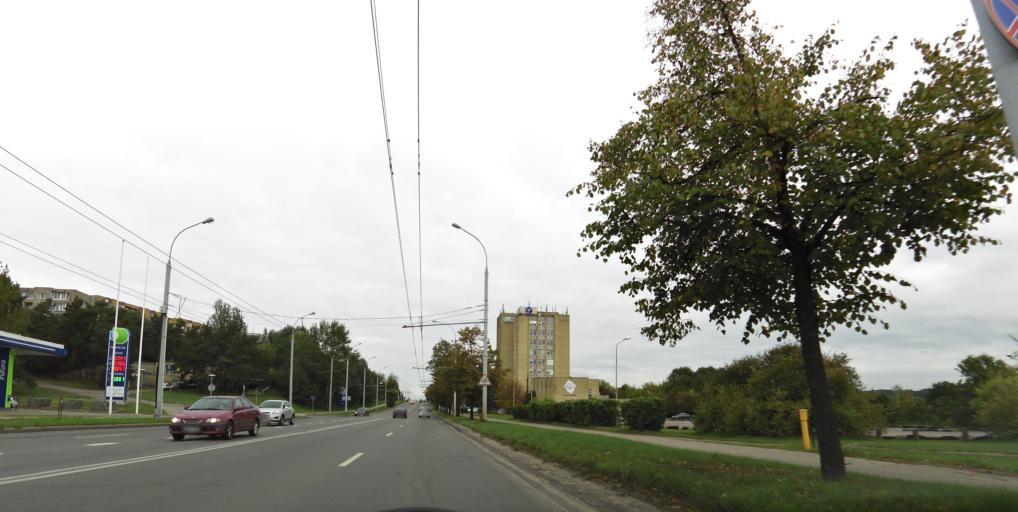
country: LT
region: Vilnius County
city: Rasos
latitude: 54.7064
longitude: 25.3046
